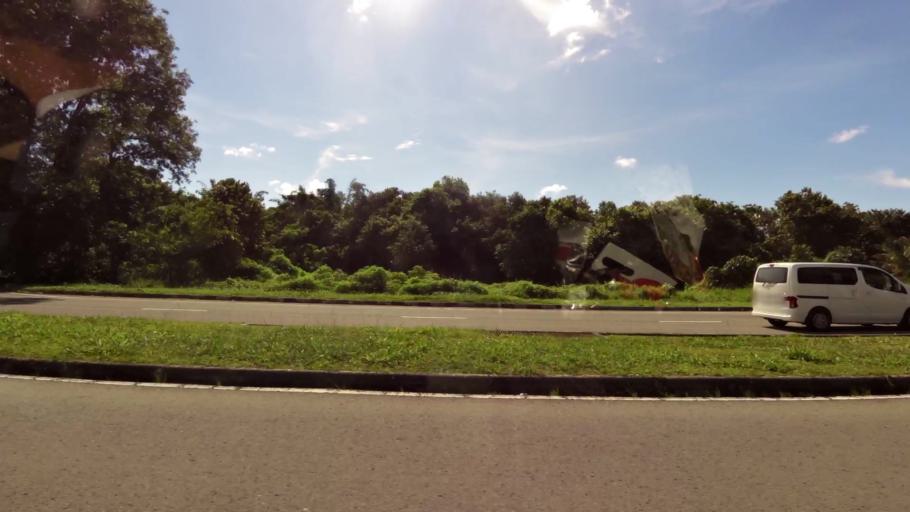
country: BN
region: Brunei and Muara
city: Bandar Seri Begawan
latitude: 4.9464
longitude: 114.9419
